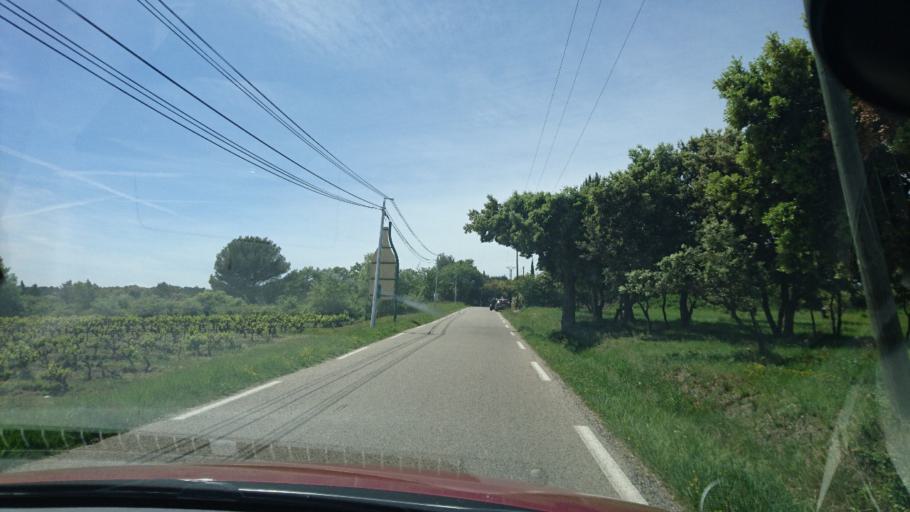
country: FR
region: Provence-Alpes-Cote d'Azur
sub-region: Departement du Vaucluse
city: Bedoin
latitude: 44.1301
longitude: 5.1748
